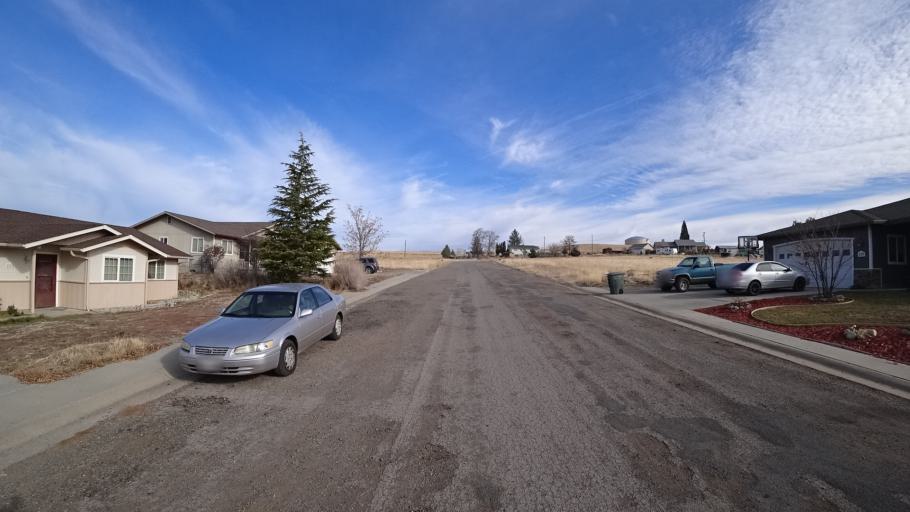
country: US
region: California
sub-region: Siskiyou County
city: Montague
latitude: 41.7295
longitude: -122.5170
